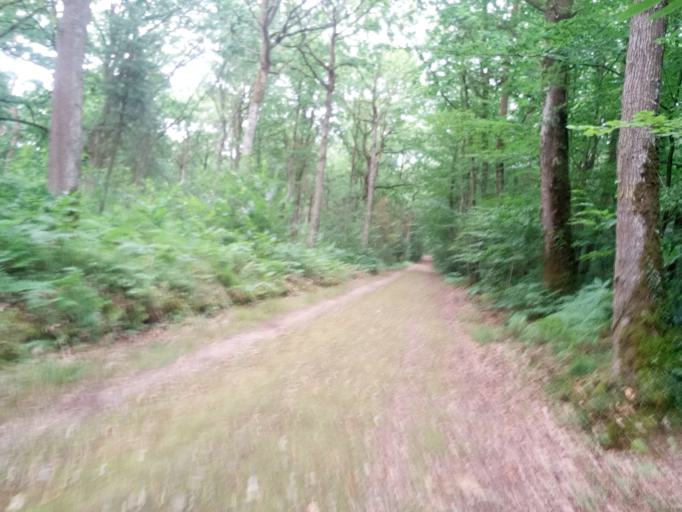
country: FR
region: Lower Normandy
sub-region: Departement du Calvados
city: Clinchamps-sur-Orne
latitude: 49.0381
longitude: -0.4359
